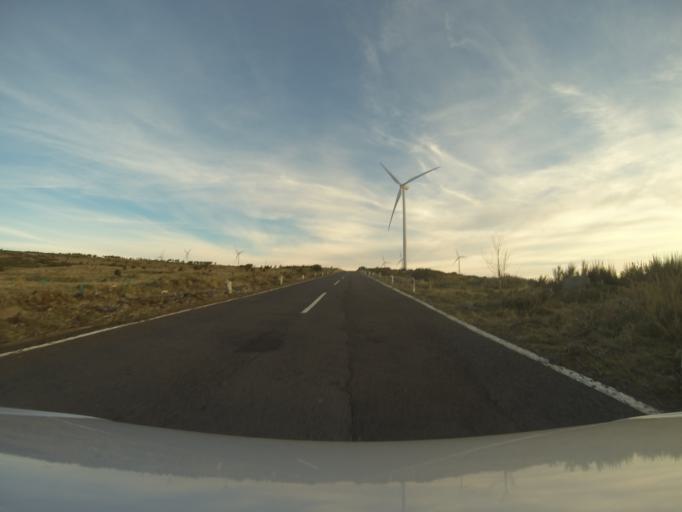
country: PT
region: Madeira
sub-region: Sao Vicente
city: Sao Vicente
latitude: 32.7494
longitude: -17.0580
